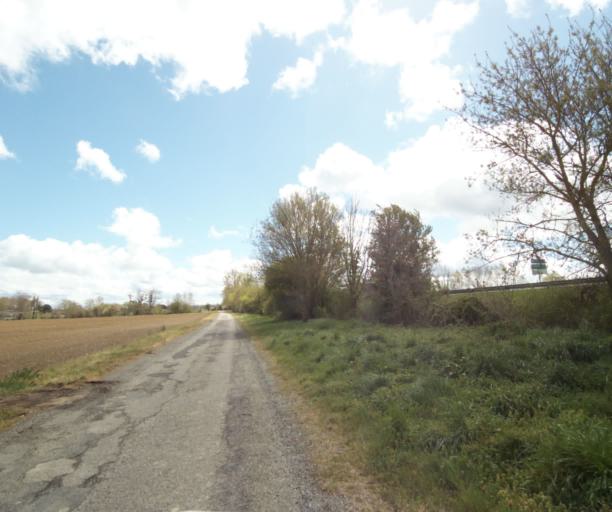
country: FR
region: Midi-Pyrenees
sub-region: Departement de l'Ariege
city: Saverdun
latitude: 43.2495
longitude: 1.5690
